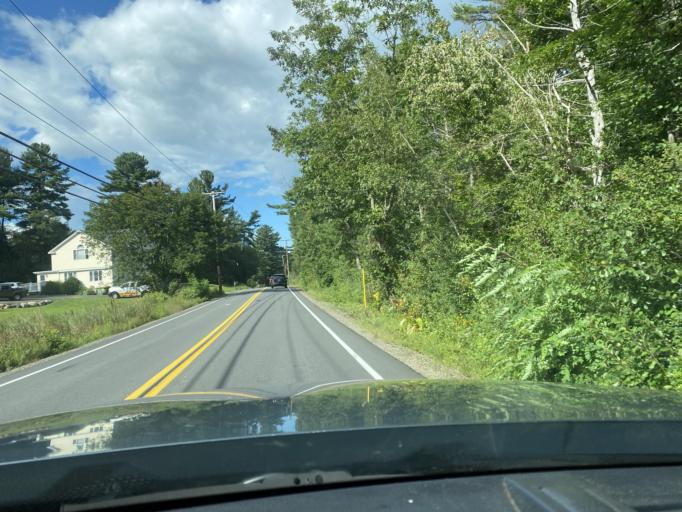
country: US
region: Maine
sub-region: York County
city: York Harbor
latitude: 43.1559
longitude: -70.7113
